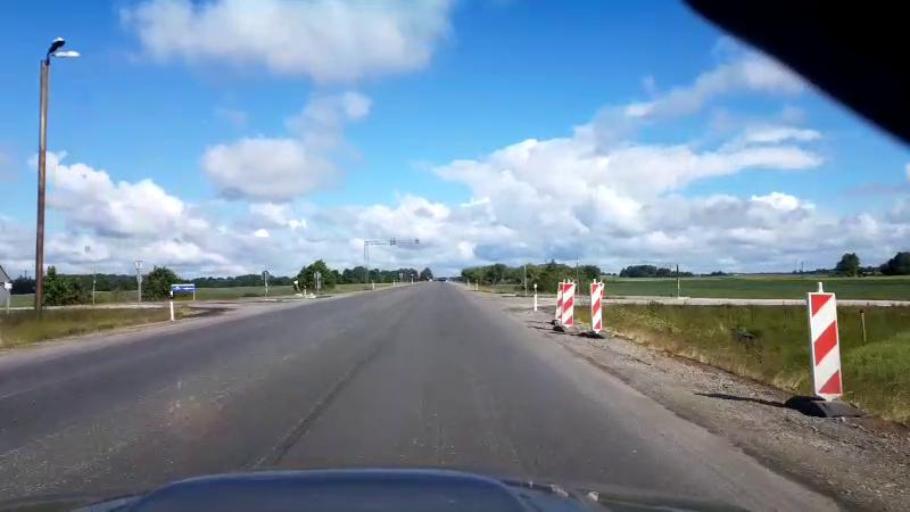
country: LV
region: Bauskas Rajons
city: Bauska
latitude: 56.3833
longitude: 24.2578
